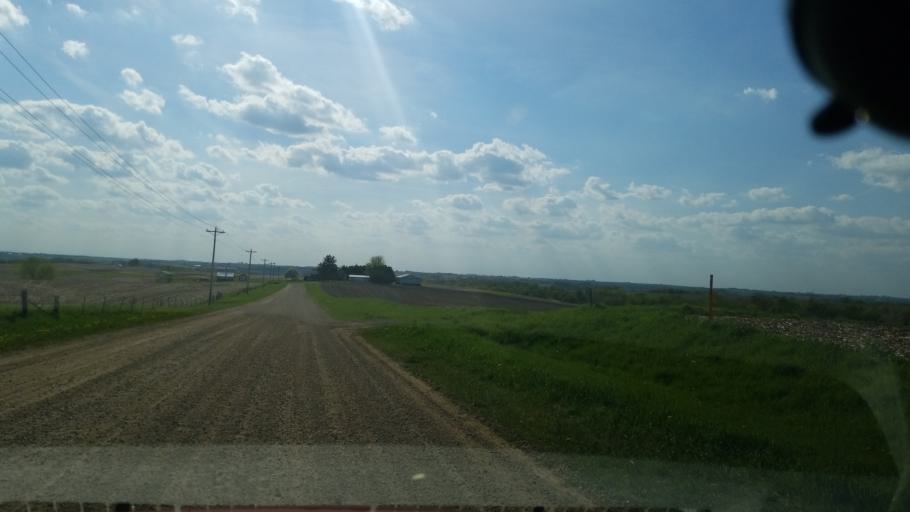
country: US
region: Iowa
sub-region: Jackson County
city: Maquoketa
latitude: 42.2150
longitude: -90.7236
